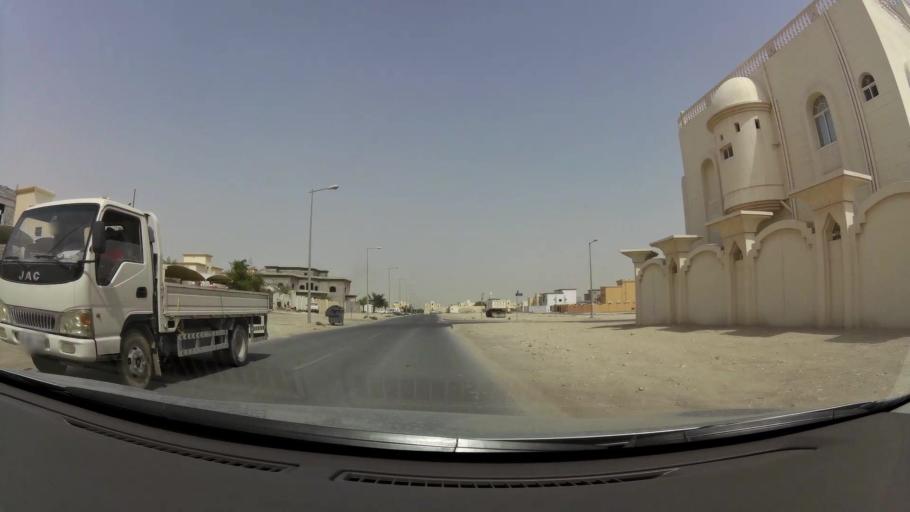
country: QA
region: Baladiyat ar Rayyan
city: Ar Rayyan
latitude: 25.2380
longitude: 51.3777
